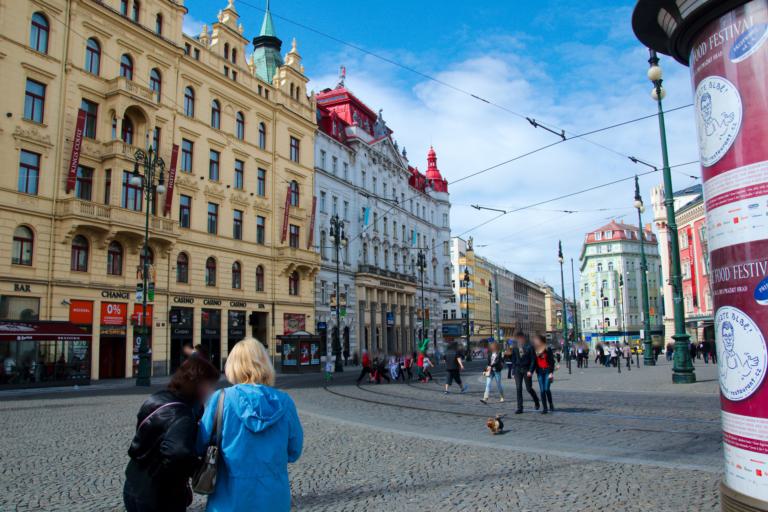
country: CZ
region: Praha
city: Prague
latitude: 50.0881
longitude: 14.4286
